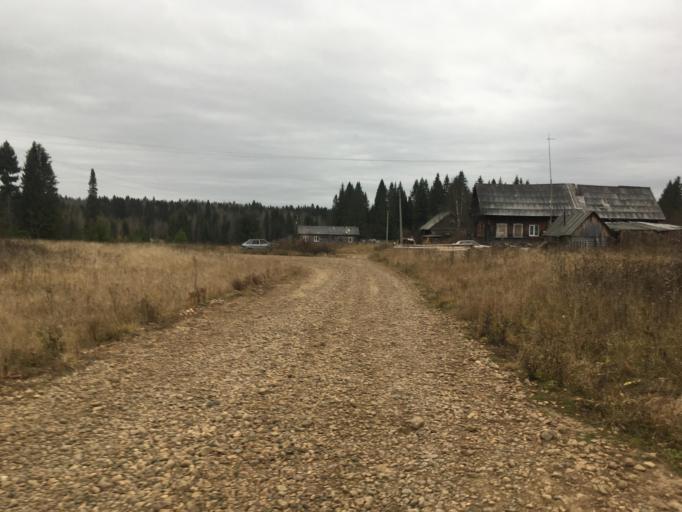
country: RU
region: Perm
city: Komarikhinskiy
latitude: 58.0887
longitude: 57.1090
